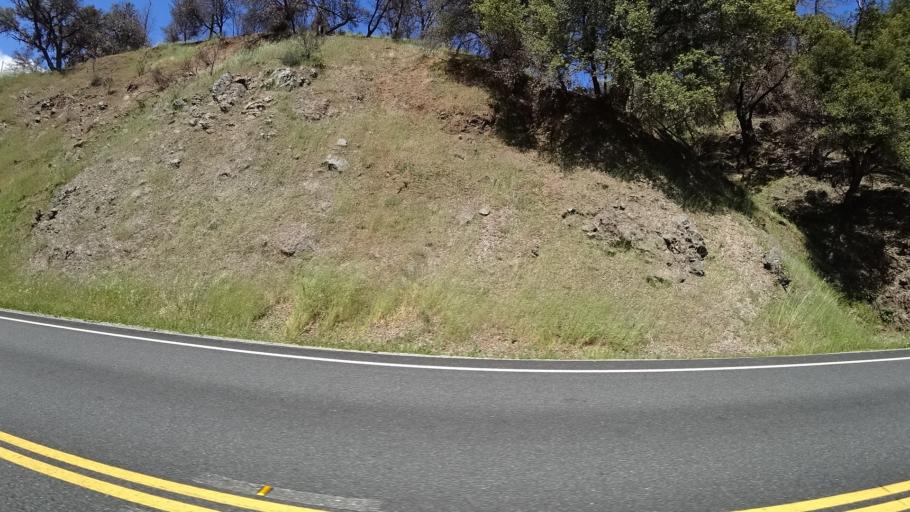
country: US
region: California
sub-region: Trinity County
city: Weaverville
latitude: 40.7669
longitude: -123.1134
